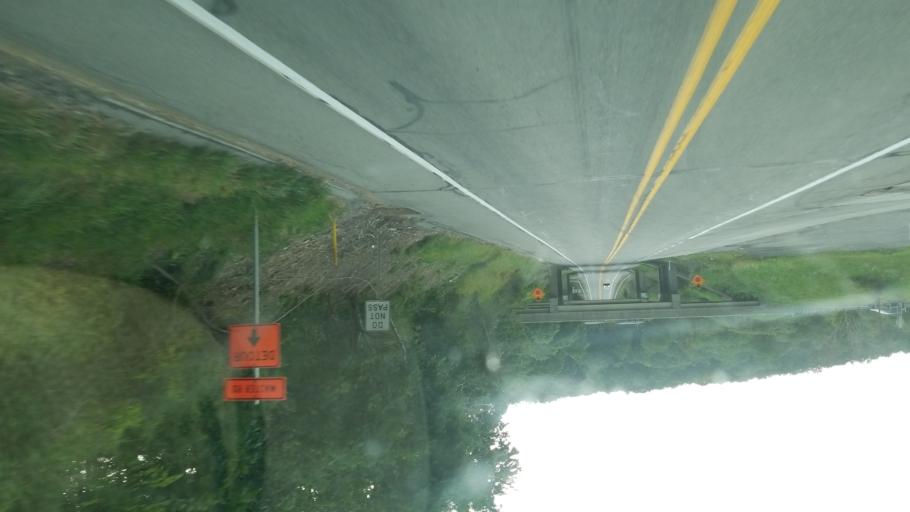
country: US
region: Pennsylvania
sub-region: Clarion County
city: Knox
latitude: 41.1828
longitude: -79.6741
